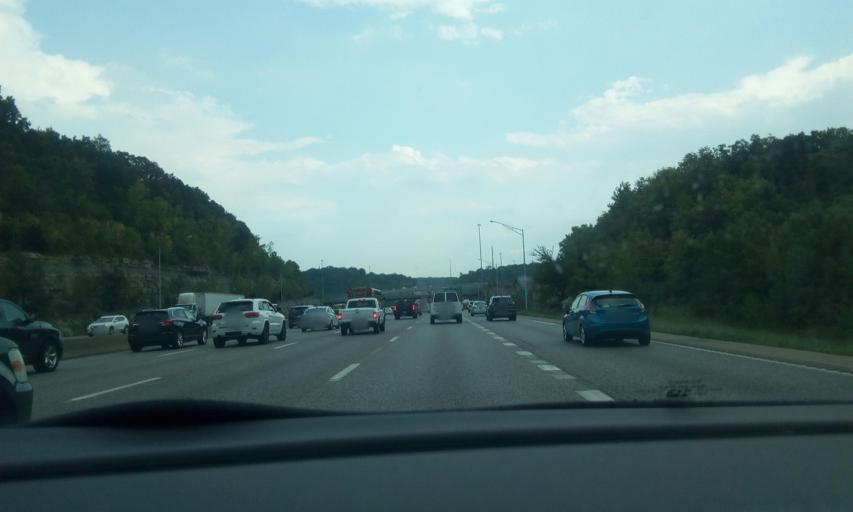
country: US
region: Missouri
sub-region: Saint Louis County
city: Sunset Hills
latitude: 38.5541
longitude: -90.4323
